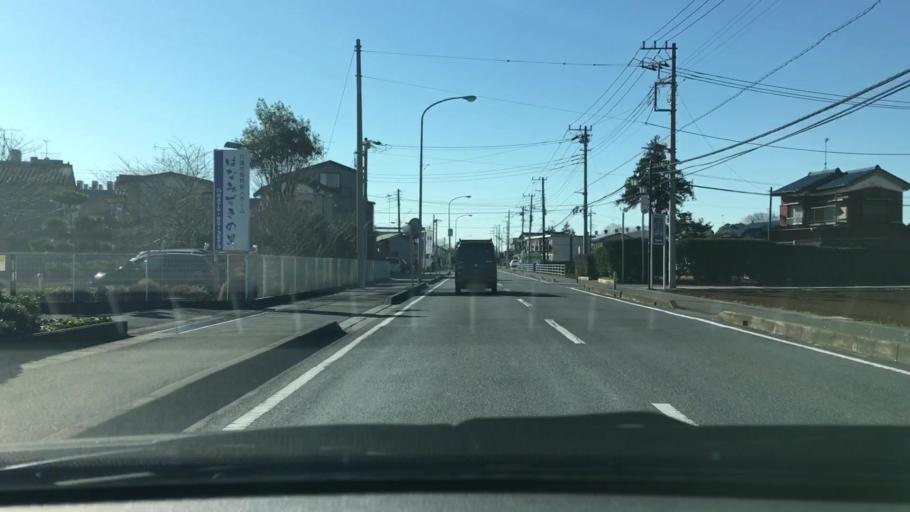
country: JP
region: Chiba
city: Narita
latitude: 35.7267
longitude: 140.3372
